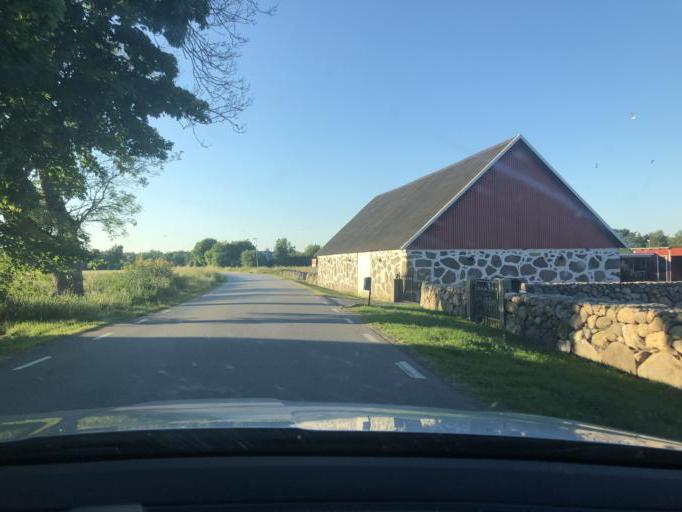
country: SE
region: Blekinge
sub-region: Karlshamns Kommun
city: Morrum
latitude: 56.1289
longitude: 14.6689
